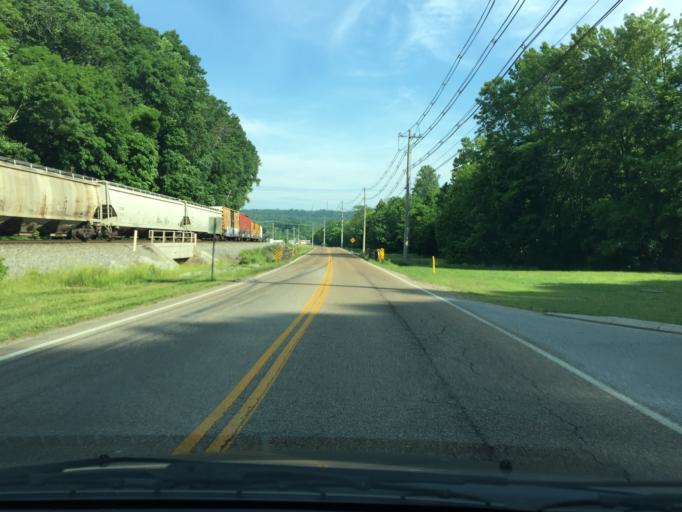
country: US
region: Tennessee
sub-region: Hamilton County
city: Collegedale
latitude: 35.0468
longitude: -85.0360
